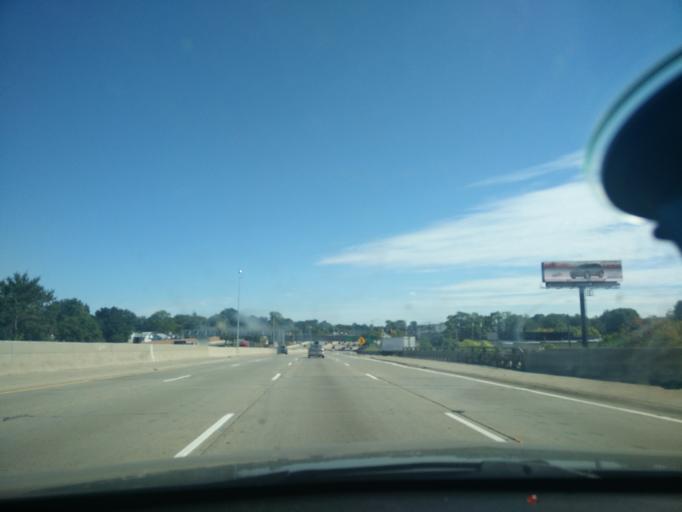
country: US
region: Michigan
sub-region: Oakland County
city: Madison Heights
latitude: 42.4767
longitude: -83.1092
